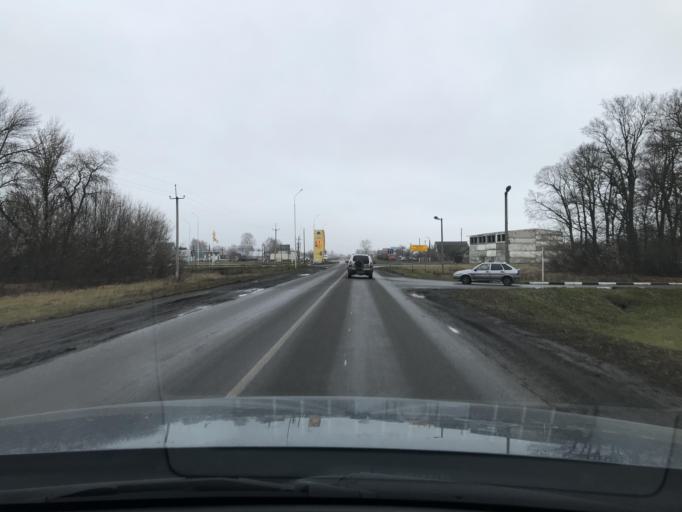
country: RU
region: Penza
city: Zemetchino
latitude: 53.5111
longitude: 42.6403
